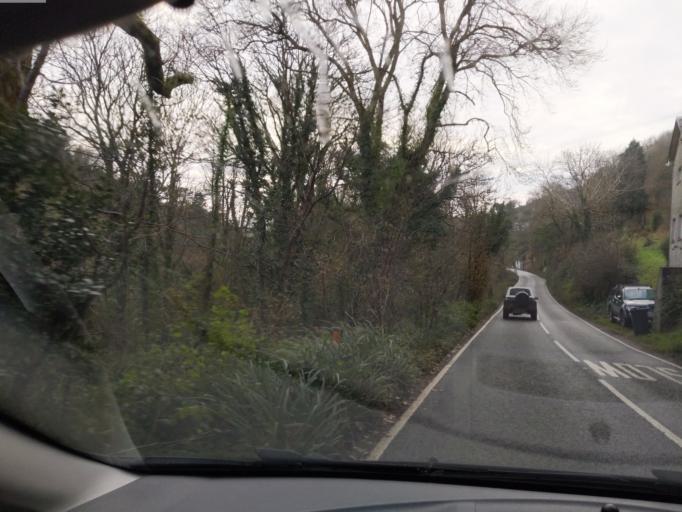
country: GB
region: England
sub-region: Cornwall
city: Looe
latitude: 50.3714
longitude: -4.3875
